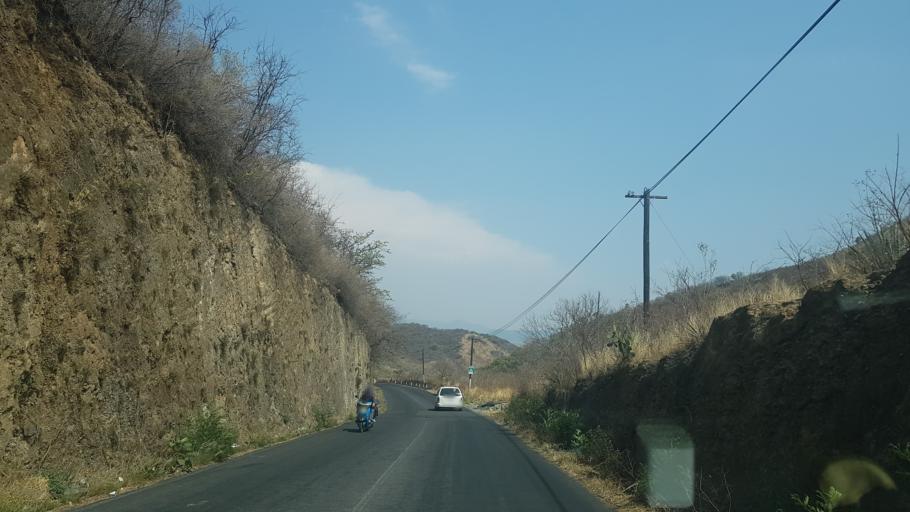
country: MX
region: Puebla
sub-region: Tianguismanalco
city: San Martin Tlapala
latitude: 18.9476
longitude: -98.4591
